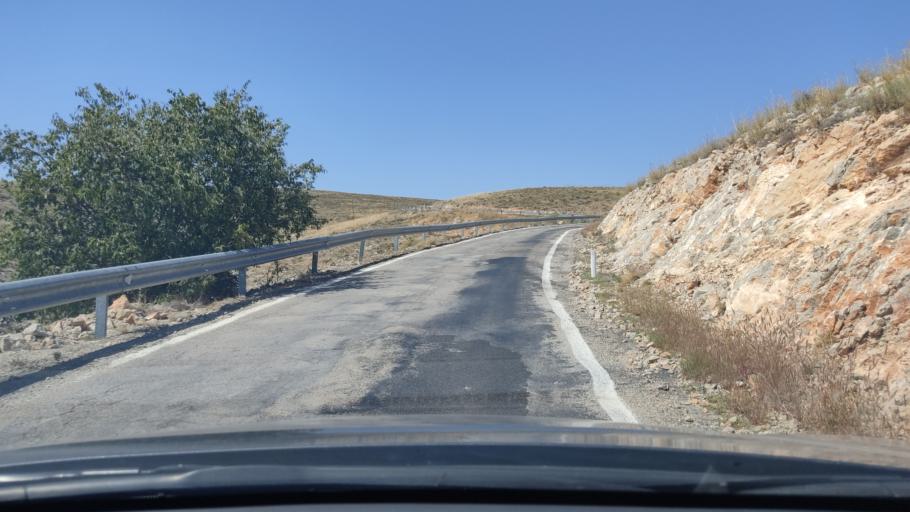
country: ES
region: Aragon
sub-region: Provincia de Teruel
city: Huesa del Comun
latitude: 41.0204
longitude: -0.9531
